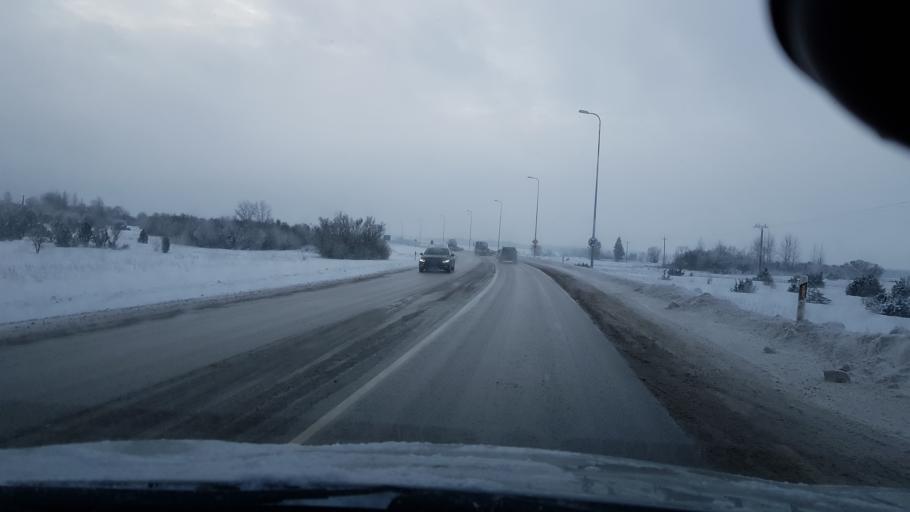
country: EE
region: Harju
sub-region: Saue linn
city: Saue
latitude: 59.3602
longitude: 24.4954
